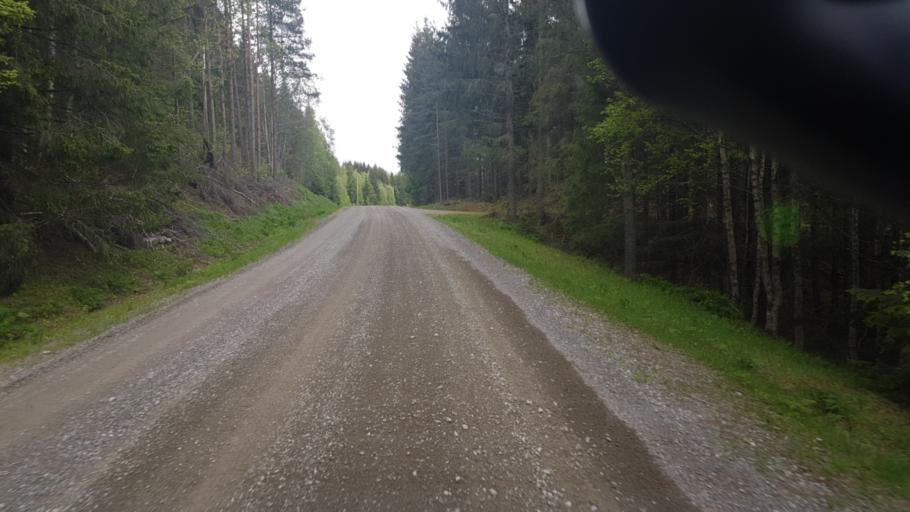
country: SE
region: Vaermland
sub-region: Arvika Kommun
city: Arvika
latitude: 59.8575
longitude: 12.7149
